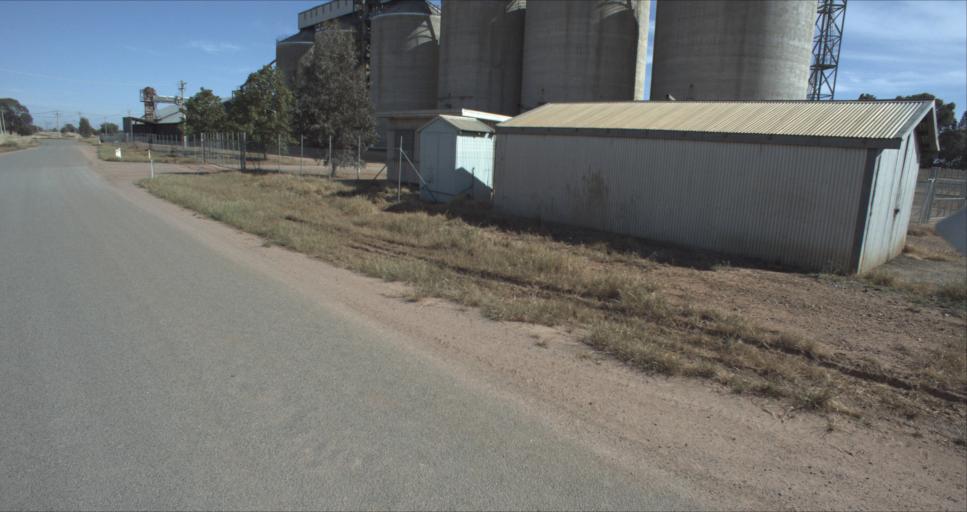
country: AU
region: New South Wales
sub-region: Leeton
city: Leeton
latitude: -34.6058
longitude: 146.4066
